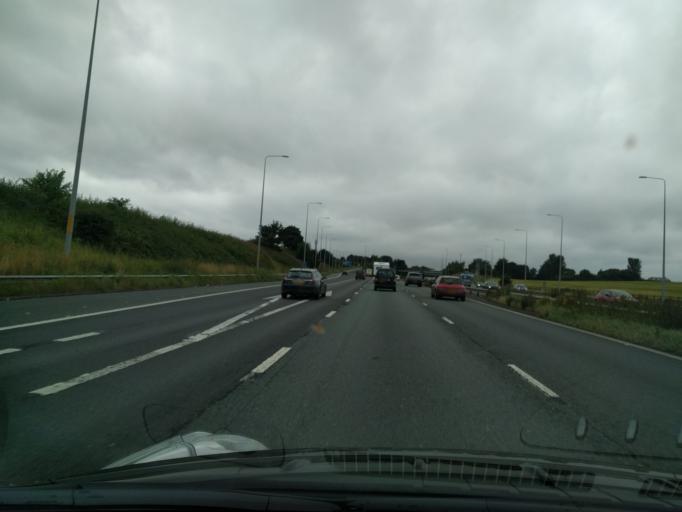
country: GB
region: England
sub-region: Warrington
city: Winwick
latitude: 53.4371
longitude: -2.5780
